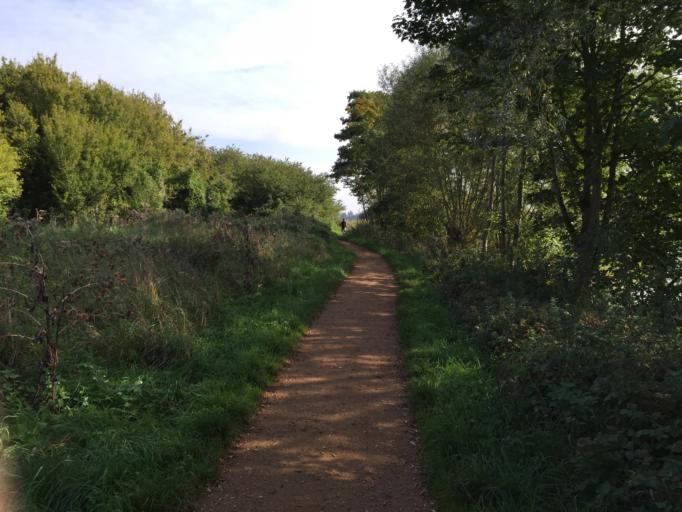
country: GB
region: England
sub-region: West Berkshire
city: Eton
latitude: 51.4928
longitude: -0.6359
